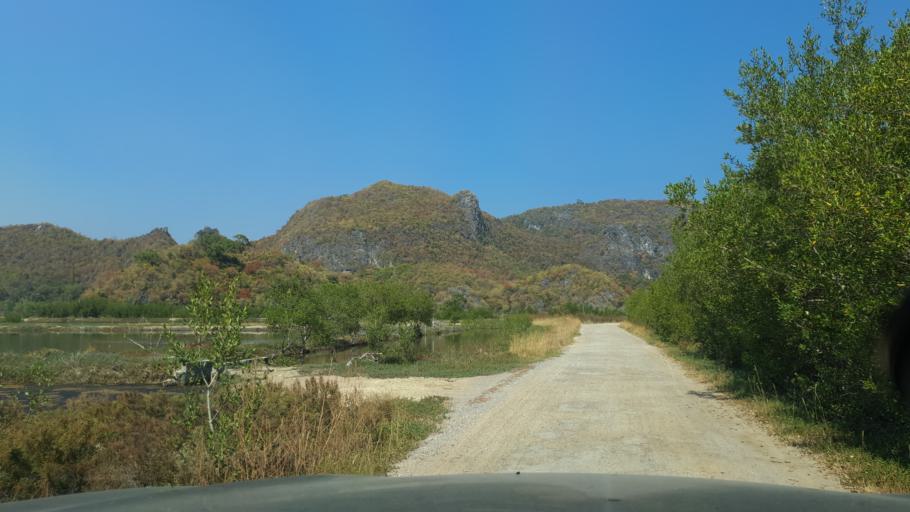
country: TH
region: Prachuap Khiri Khan
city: Sam Roi Yot
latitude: 12.1967
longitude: 99.9912
